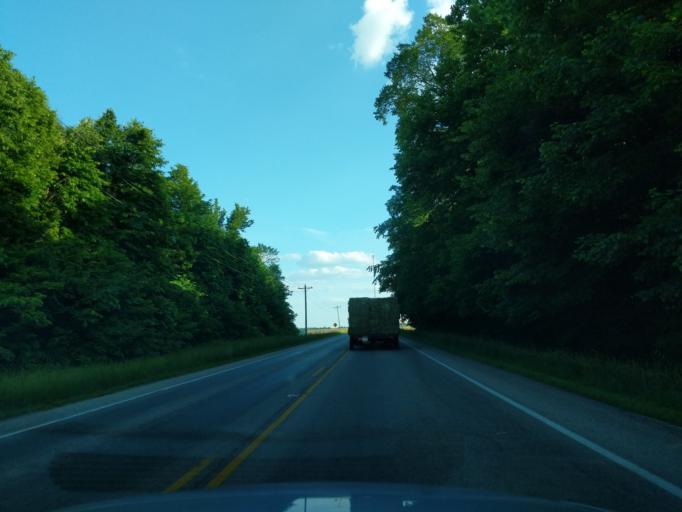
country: US
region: Indiana
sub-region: Huntington County
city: Roanoke
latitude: 41.0082
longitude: -85.4707
